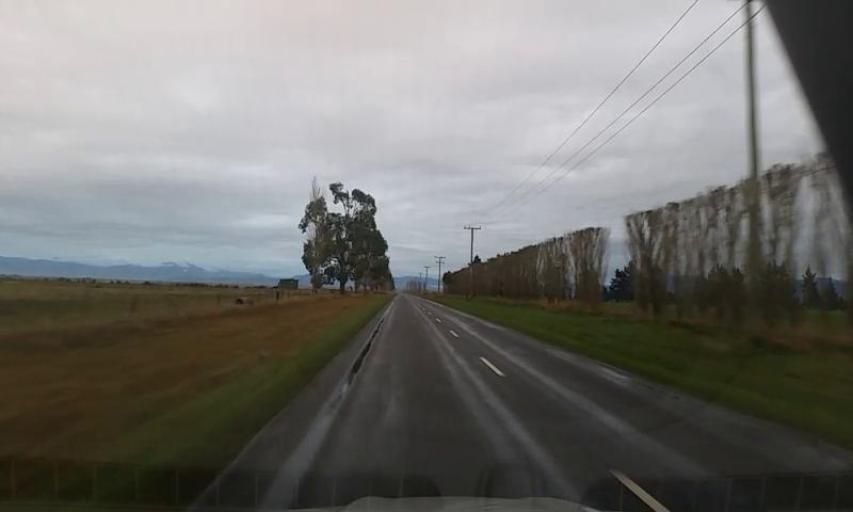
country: NZ
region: Canterbury
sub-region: Ashburton District
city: Methven
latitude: -43.7391
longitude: 171.6773
